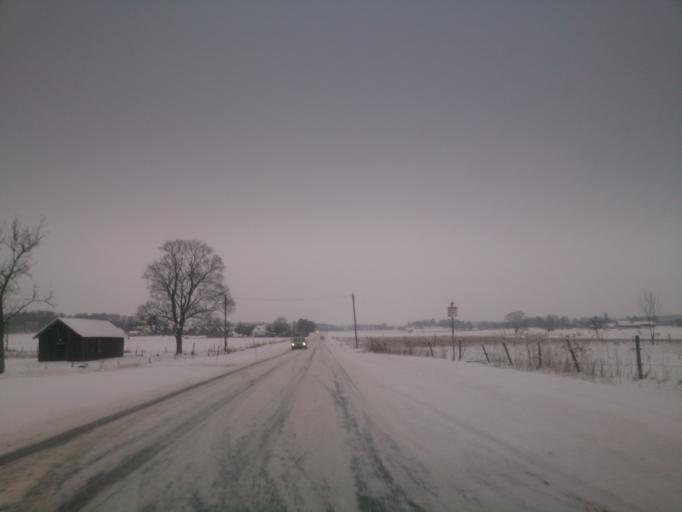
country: SE
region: OEstergoetland
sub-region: Norrkopings Kommun
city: Kimstad
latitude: 58.5644
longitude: 15.9458
